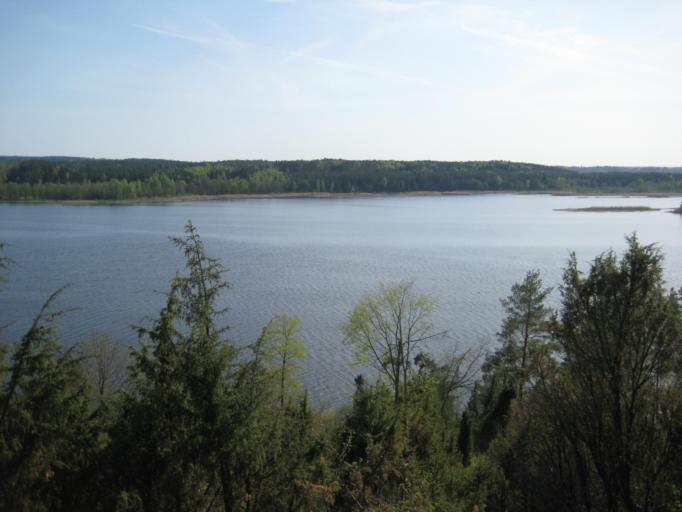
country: LT
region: Kauno apskritis
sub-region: Kauno rajonas
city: Karmelava
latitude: 54.8122
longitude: 24.1825
